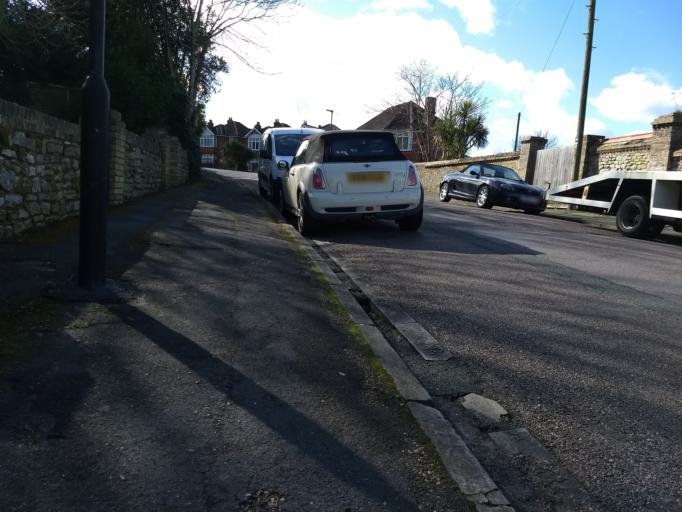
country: GB
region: England
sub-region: Isle of Wight
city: Ryde
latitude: 50.7242
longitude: -1.1514
